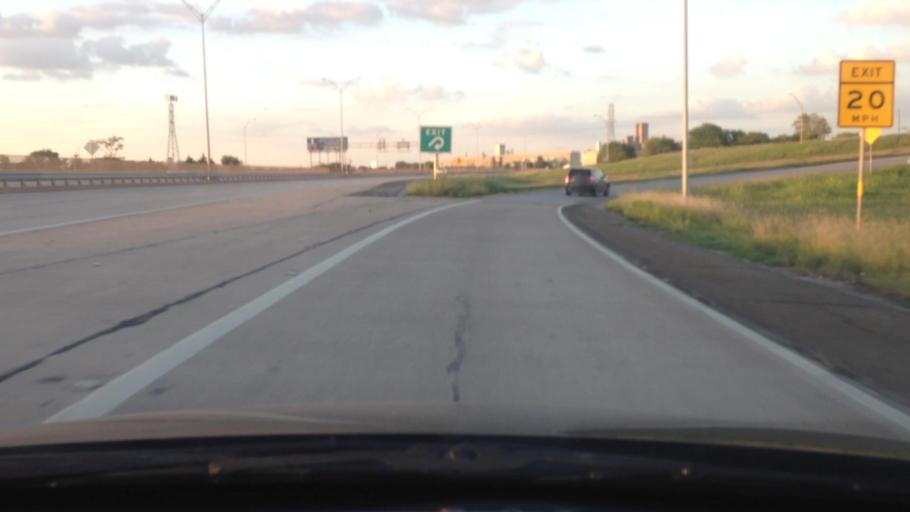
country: US
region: Texas
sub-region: Tarrant County
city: Saginaw
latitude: 32.8377
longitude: -97.3627
